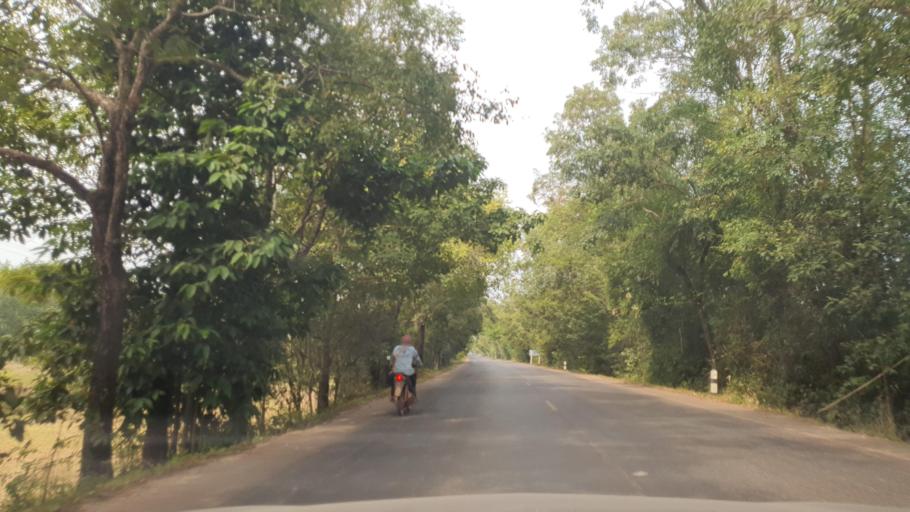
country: TH
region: Changwat Bueng Kan
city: Bung Khla
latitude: 18.2049
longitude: 104.0496
